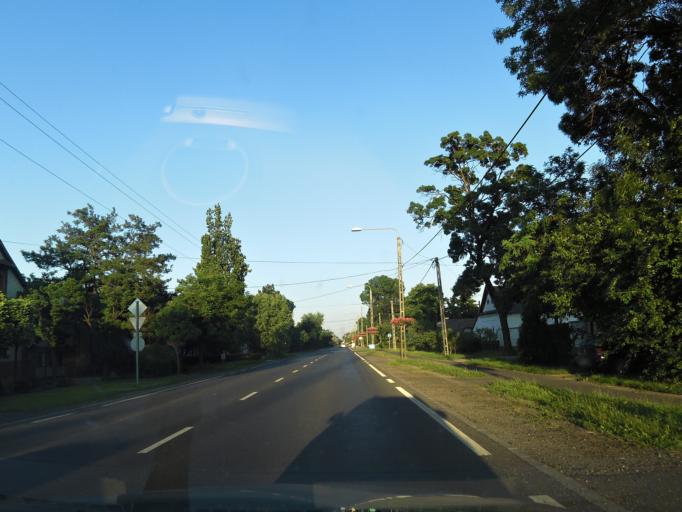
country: HU
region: Csongrad
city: Hodmezovasarhely
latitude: 46.4300
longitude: 20.3204
